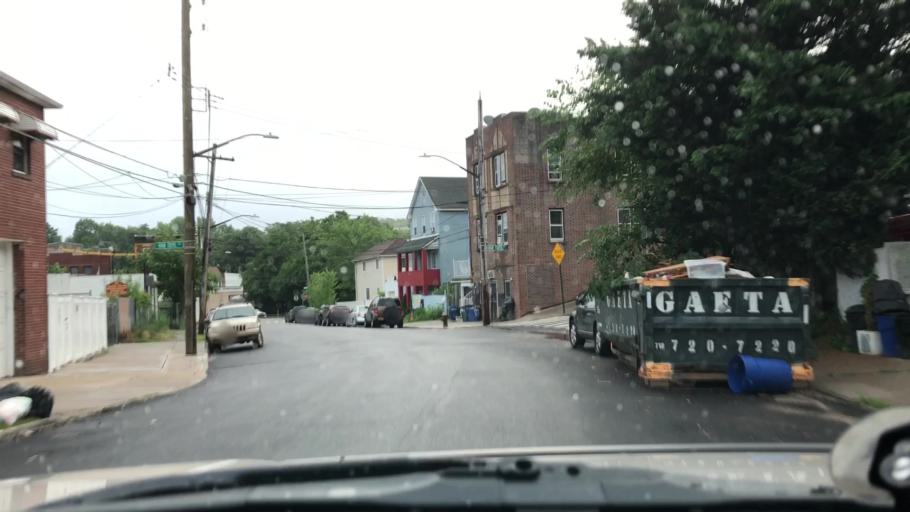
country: US
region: New Jersey
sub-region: Hudson County
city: Bayonne
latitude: 40.6387
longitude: -74.0883
